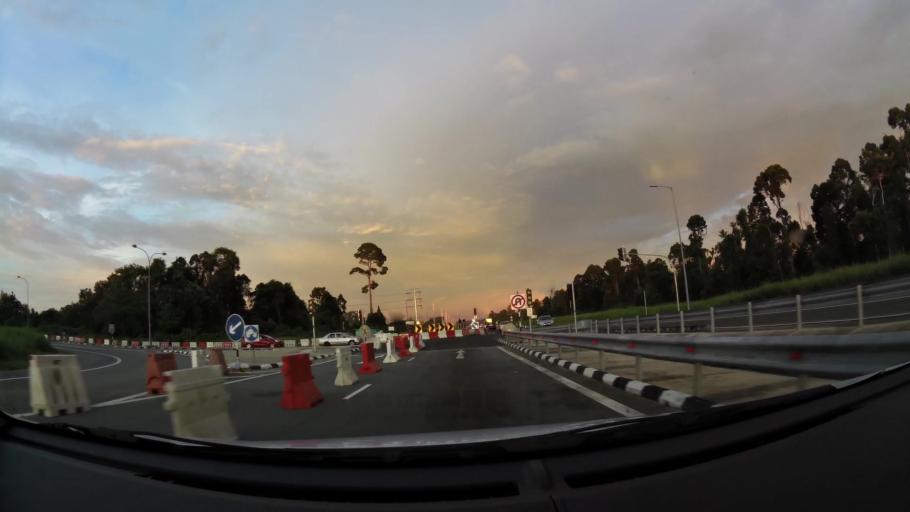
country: BN
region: Belait
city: Kuala Belait
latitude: 4.5798
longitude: 114.2593
